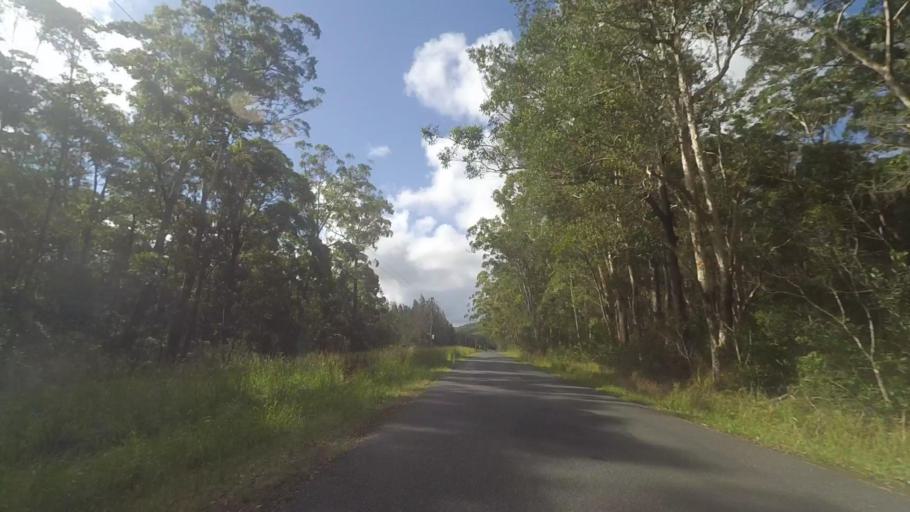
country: AU
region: New South Wales
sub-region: Great Lakes
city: Forster
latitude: -32.4041
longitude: 152.4617
